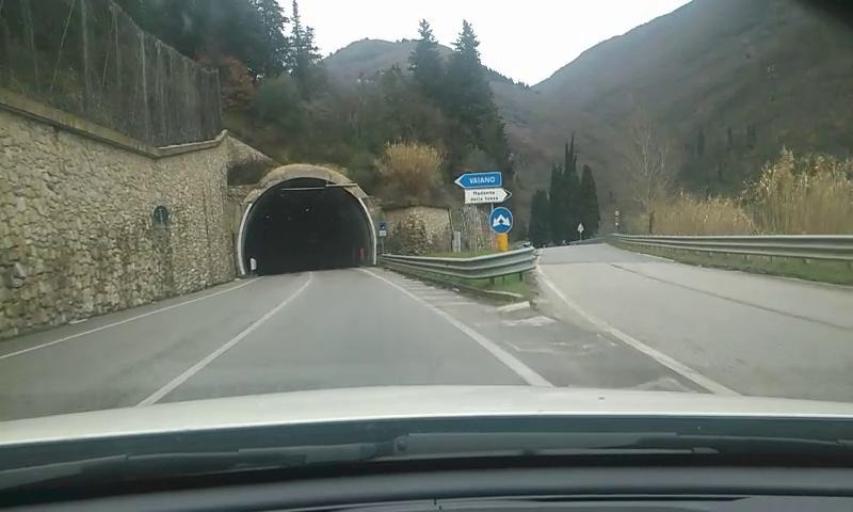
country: IT
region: Tuscany
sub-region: Provincia di Prato
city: Vaiano
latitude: 43.9133
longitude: 11.1242
